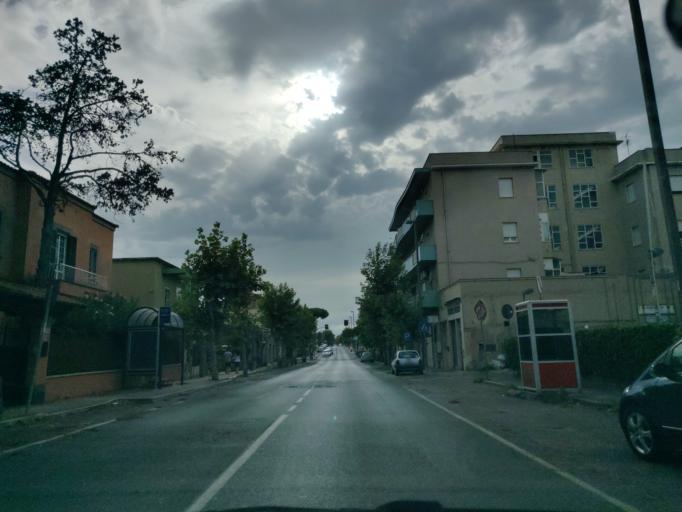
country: IT
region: Latium
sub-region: Citta metropolitana di Roma Capitale
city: Santa Marinella
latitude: 42.0327
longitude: 11.8484
